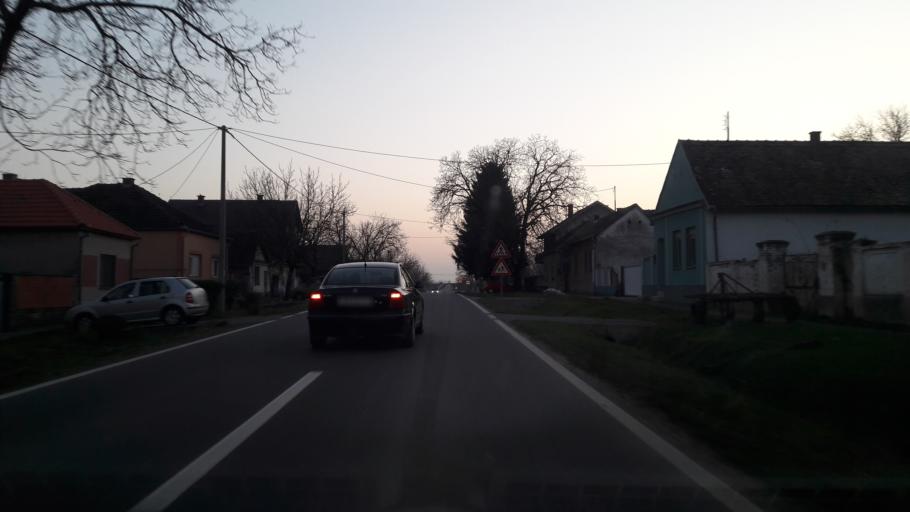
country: HR
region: Vukovarsko-Srijemska
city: Slakovci
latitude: 45.2225
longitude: 18.9885
